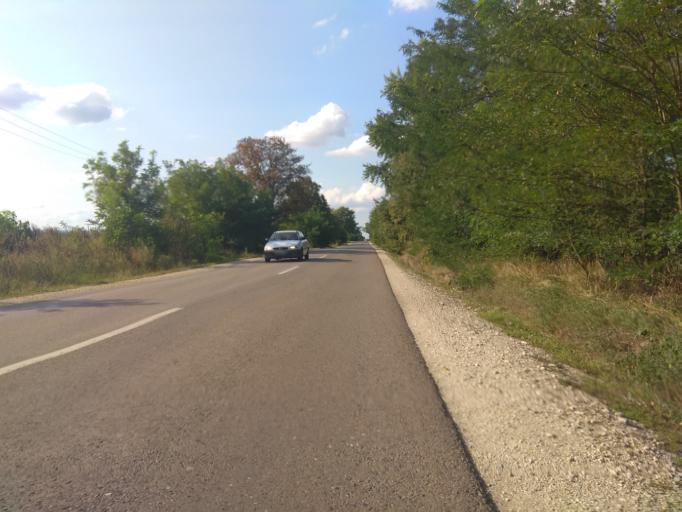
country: HU
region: Borsod-Abauj-Zemplen
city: Hejobaba
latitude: 47.8962
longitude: 20.8924
